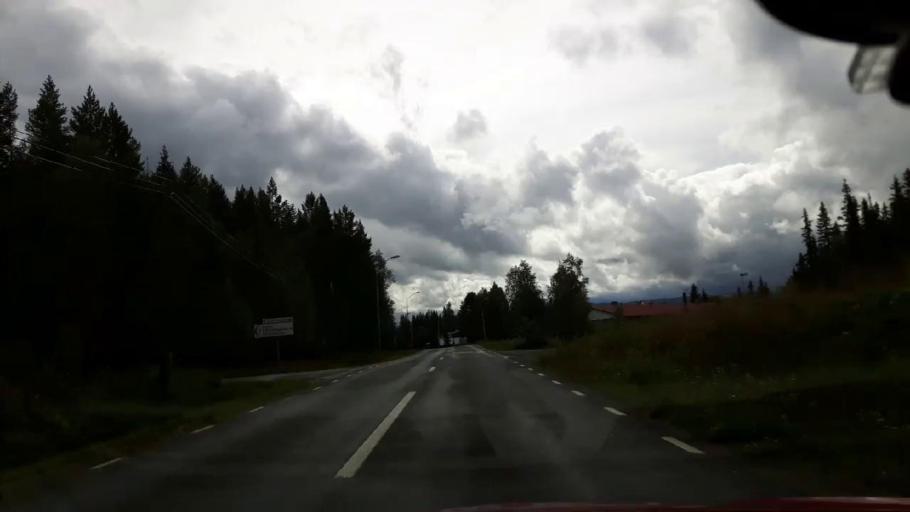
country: NO
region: Nord-Trondelag
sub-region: Lierne
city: Sandvika
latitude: 64.5067
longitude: 14.1573
